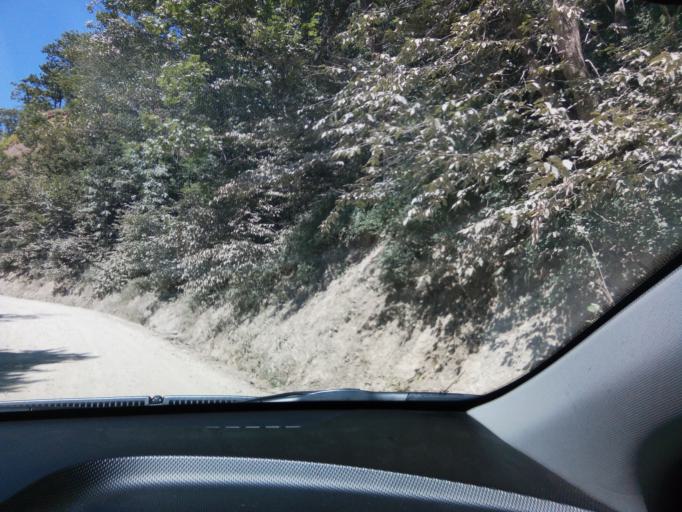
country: RU
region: Krasnodarskiy
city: Khadyzhensk
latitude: 44.3438
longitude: 39.2954
